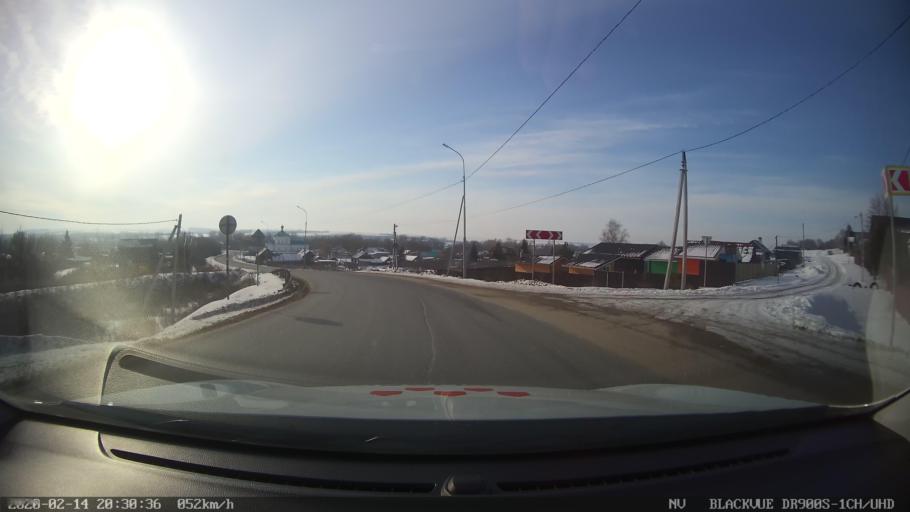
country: RU
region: Tatarstan
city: Stolbishchi
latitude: 55.4419
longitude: 48.9918
